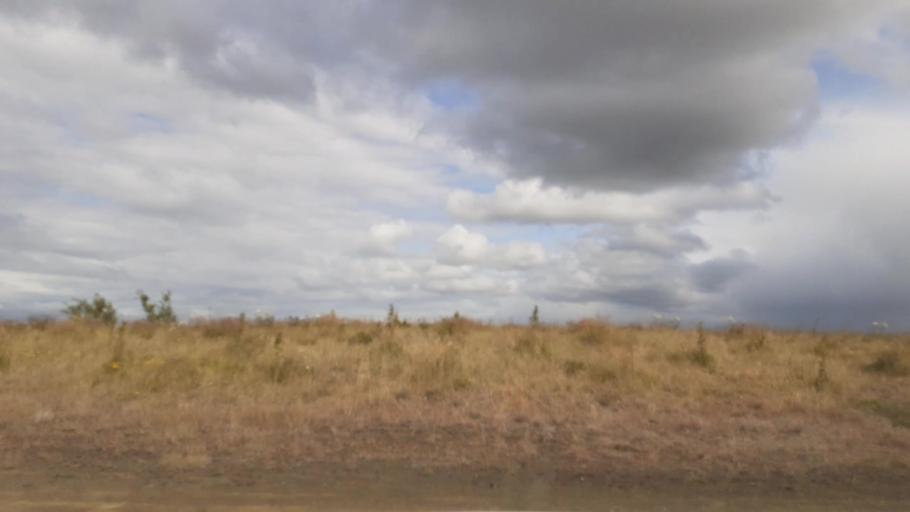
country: IS
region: South
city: Vestmannaeyjar
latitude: 63.8284
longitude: -20.4010
